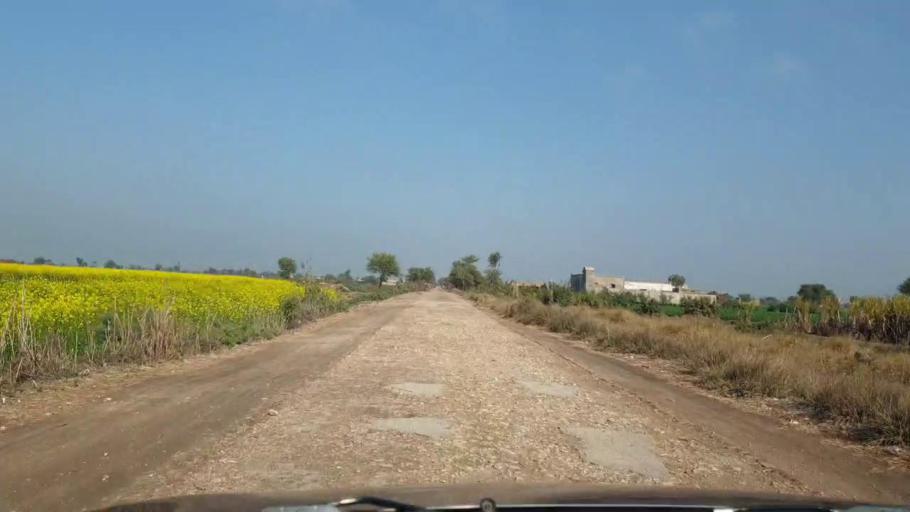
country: PK
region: Sindh
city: Sinjhoro
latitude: 26.0576
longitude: 68.7727
